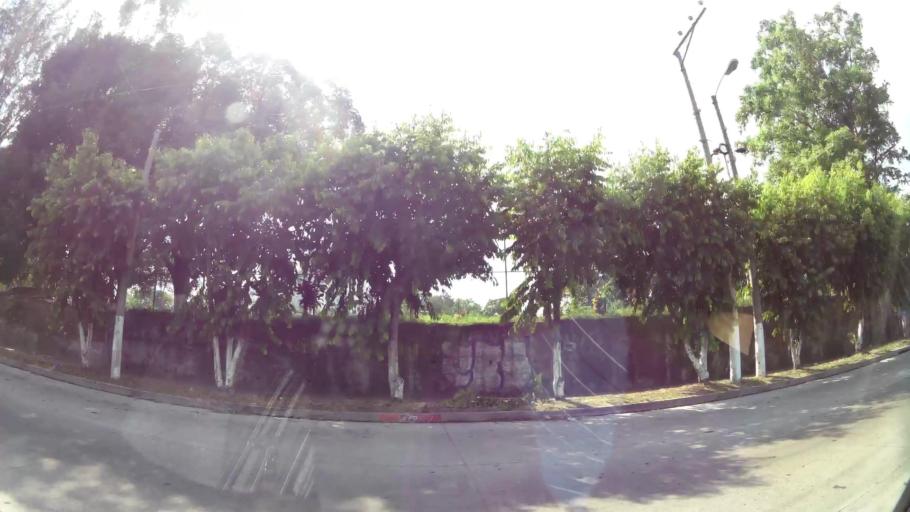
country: SV
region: San Salvador
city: Delgado
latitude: 13.7036
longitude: -89.1711
